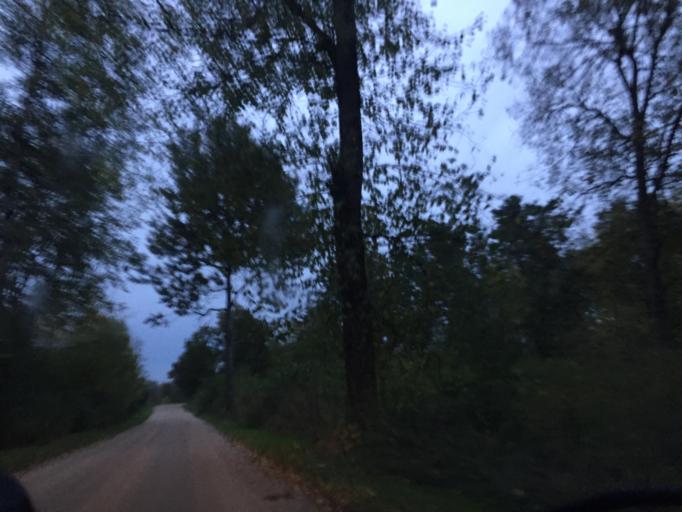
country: LV
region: Adazi
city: Adazi
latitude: 57.0816
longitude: 24.3675
